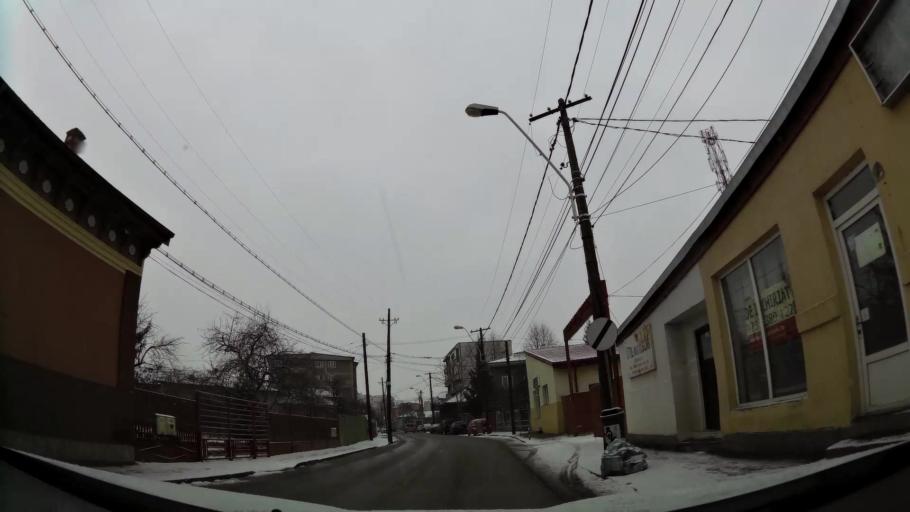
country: RO
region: Prahova
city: Ploiesti
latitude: 44.9375
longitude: 26.0172
